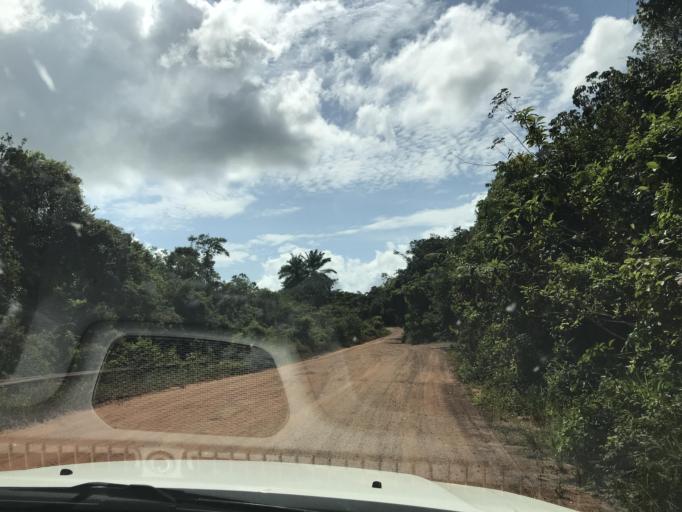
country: BR
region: Bahia
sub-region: Entre Rios
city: Entre Rios
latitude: -12.1662
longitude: -38.0720
